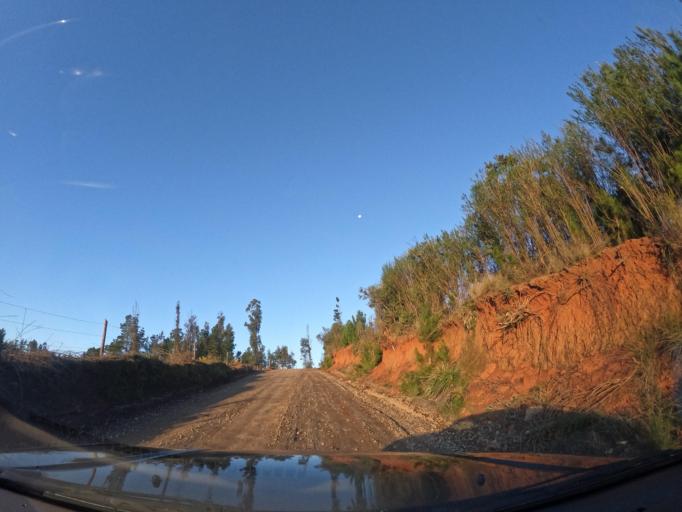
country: CL
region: Biobio
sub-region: Provincia de Concepcion
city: Chiguayante
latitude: -37.0093
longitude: -72.8937
